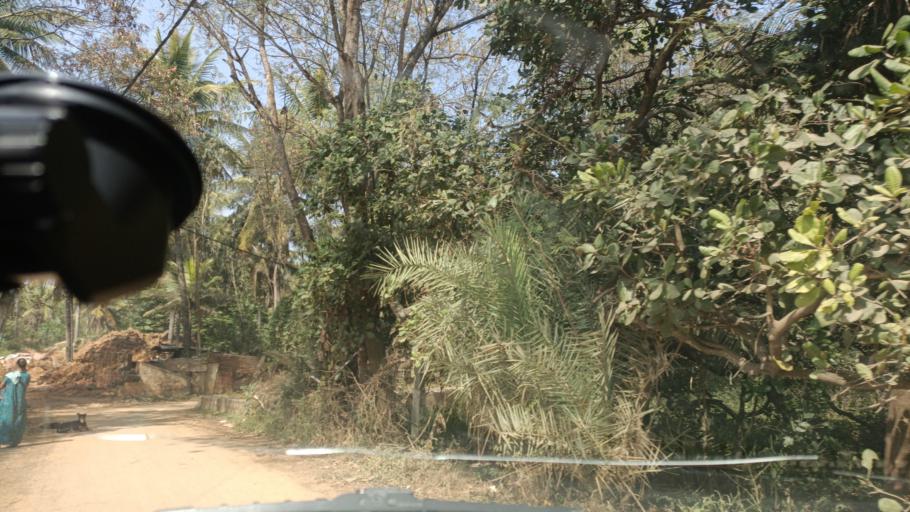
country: IN
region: Karnataka
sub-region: Bangalore Urban
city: Yelahanka
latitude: 13.1174
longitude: 77.6008
